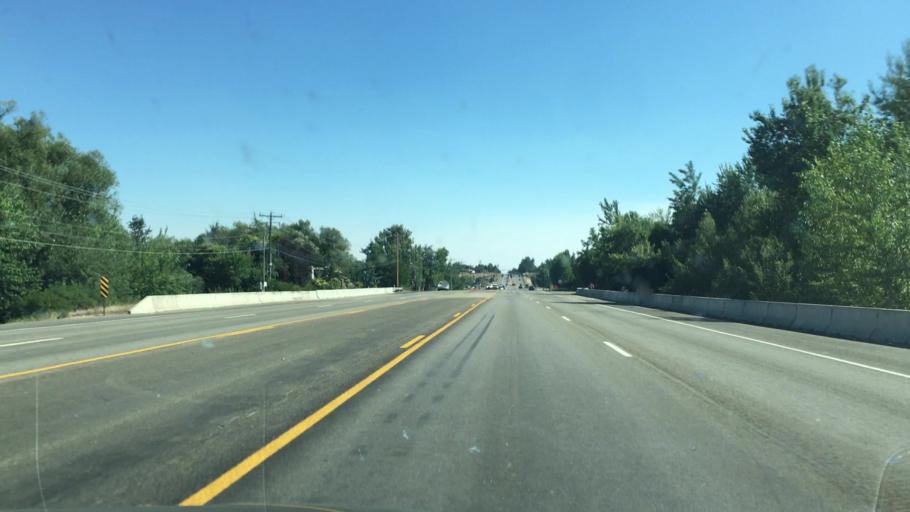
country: US
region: Idaho
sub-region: Ada County
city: Eagle
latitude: 43.6759
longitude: -116.3543
